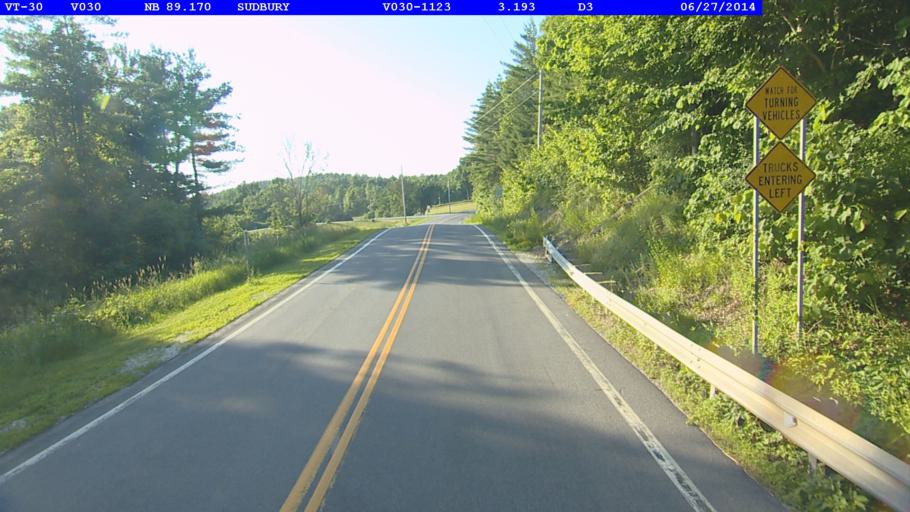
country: US
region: Vermont
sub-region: Rutland County
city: Brandon
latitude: 43.7940
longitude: -73.2050
